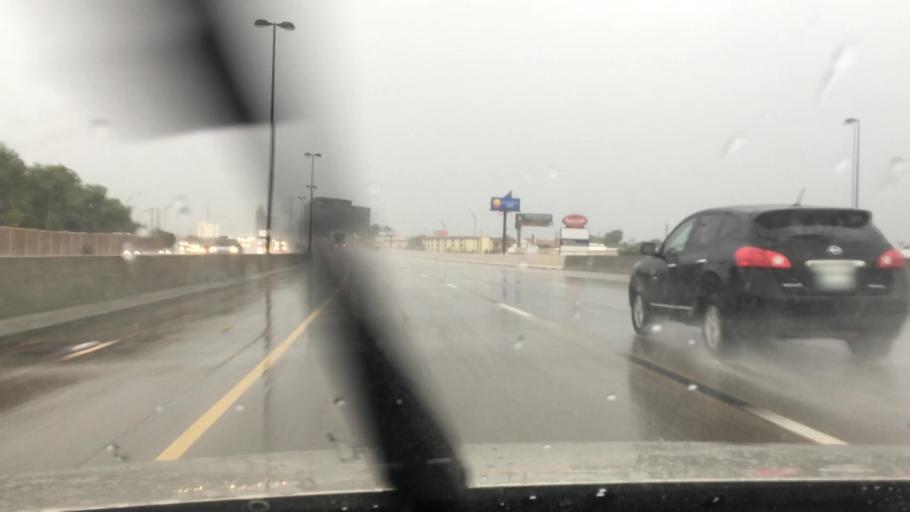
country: US
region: Oklahoma
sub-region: Tulsa County
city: Jenks
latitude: 36.0928
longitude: -95.9262
